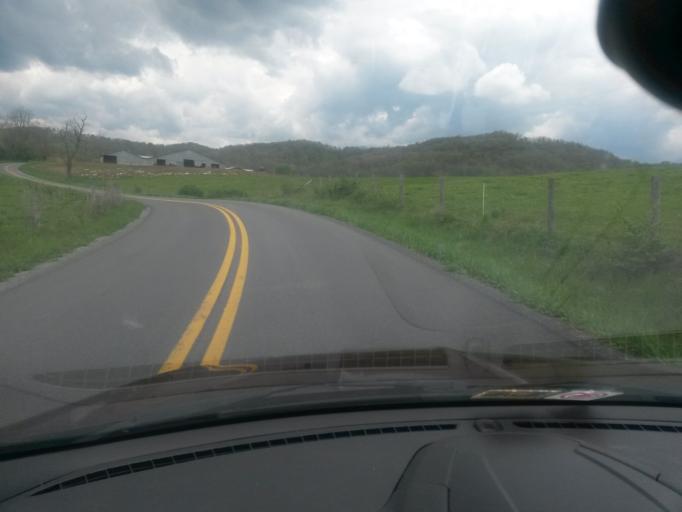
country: US
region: West Virginia
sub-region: Greenbrier County
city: Lewisburg
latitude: 37.9307
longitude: -80.3945
